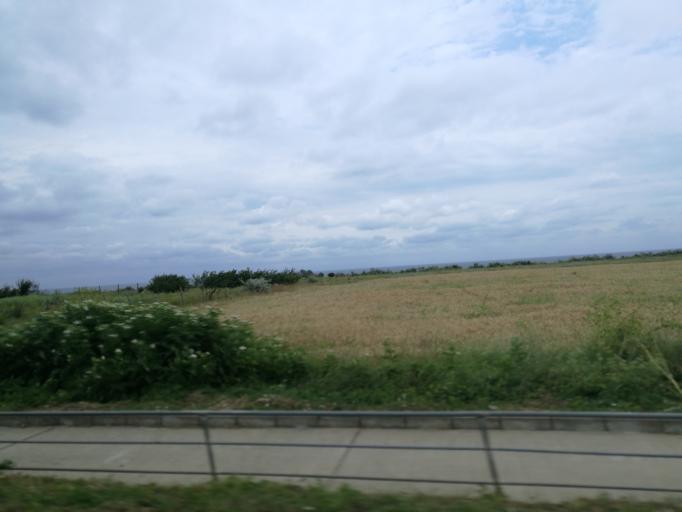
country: RO
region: Constanta
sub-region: Municipiul Mangalia
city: Mangalia
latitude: 43.7691
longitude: 28.5753
